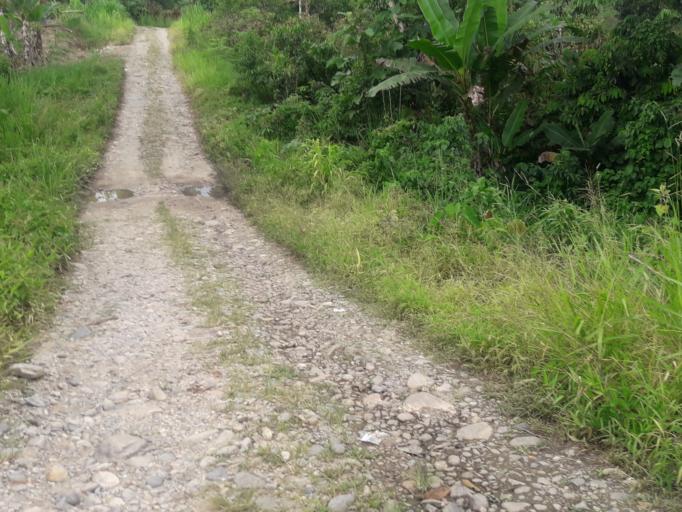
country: EC
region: Napo
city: Tena
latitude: -0.9710
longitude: -77.8409
